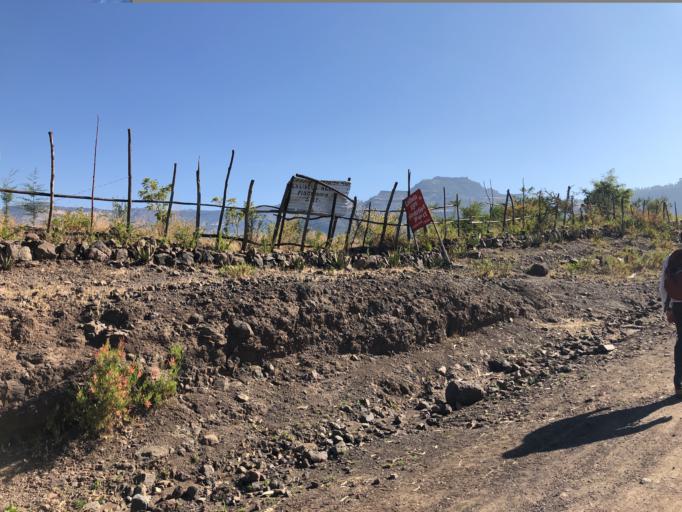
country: ET
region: Amhara
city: Lalibela
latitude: 12.0331
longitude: 39.0546
